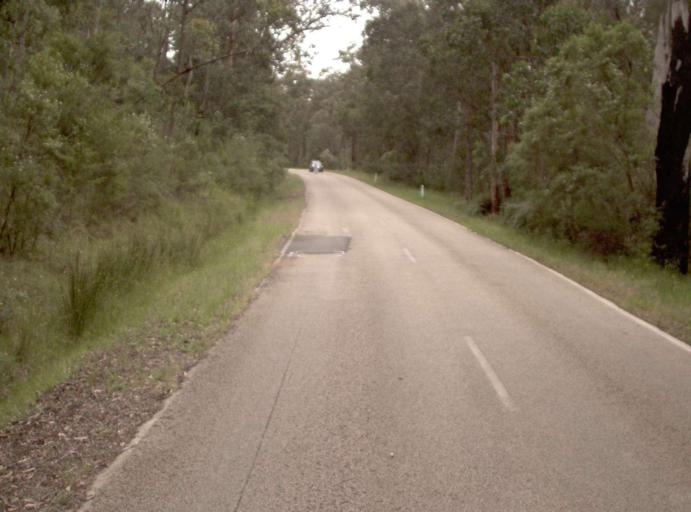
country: AU
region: Victoria
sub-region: East Gippsland
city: Bairnsdale
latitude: -37.6197
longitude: 147.1931
